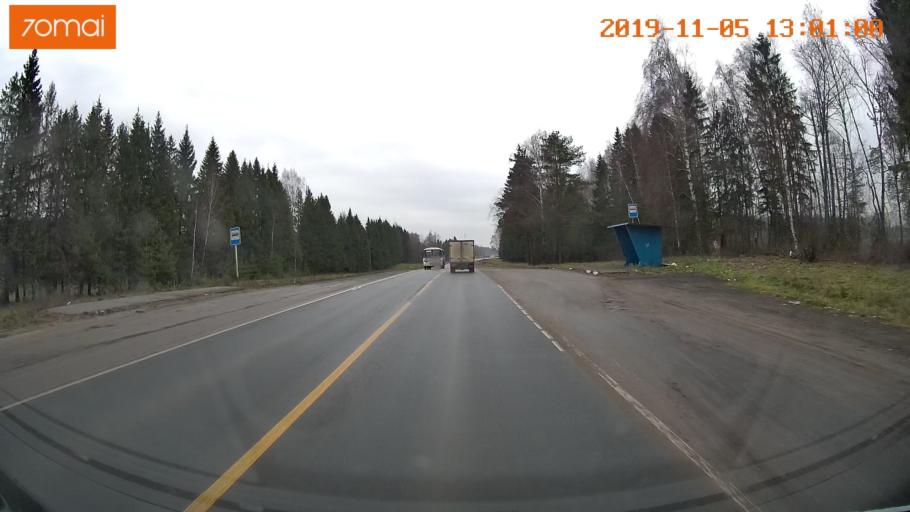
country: RU
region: Ivanovo
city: Kokhma
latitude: 56.9110
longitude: 41.1554
